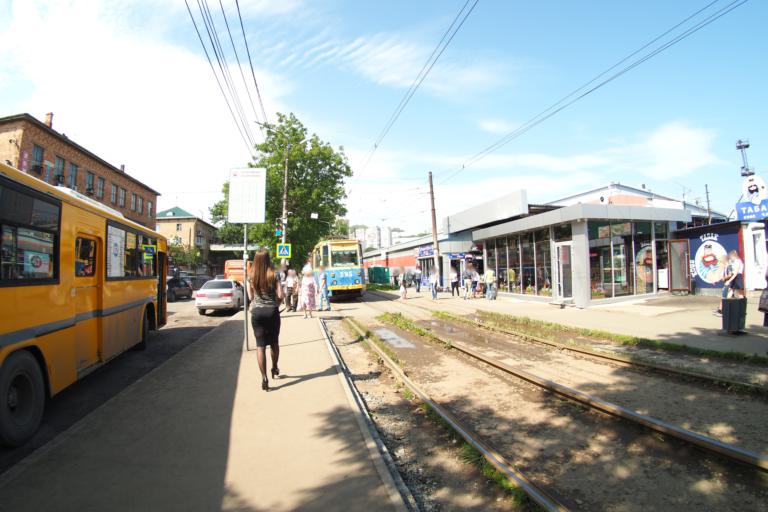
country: RU
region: Primorskiy
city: Vladivostok
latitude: 43.1052
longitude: 131.9383
